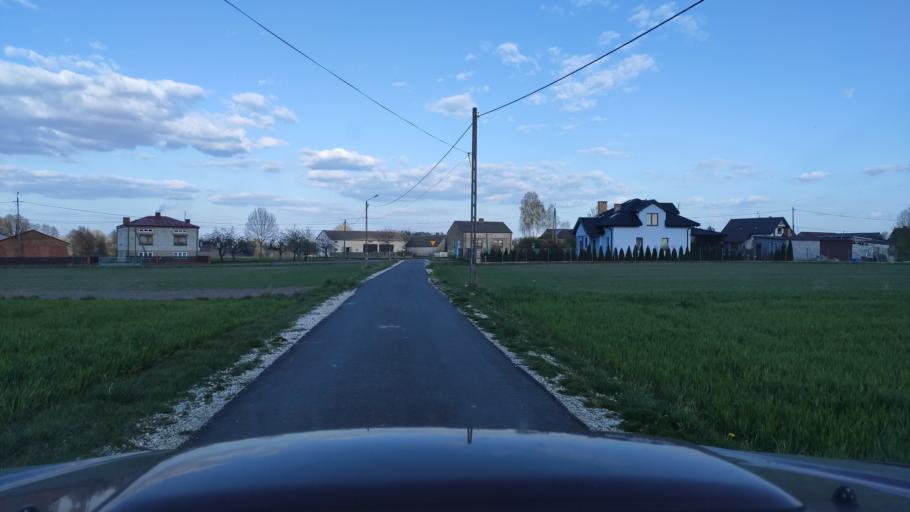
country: PL
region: Masovian Voivodeship
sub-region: Powiat zwolenski
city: Zwolen
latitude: 51.3800
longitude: 21.5785
